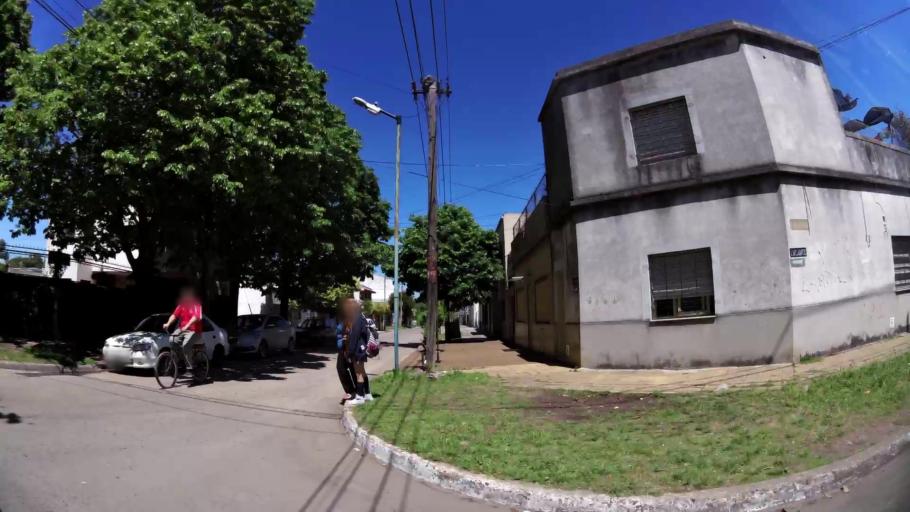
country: AR
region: Buenos Aires
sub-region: Partido de Quilmes
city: Quilmes
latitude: -34.7217
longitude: -58.2998
